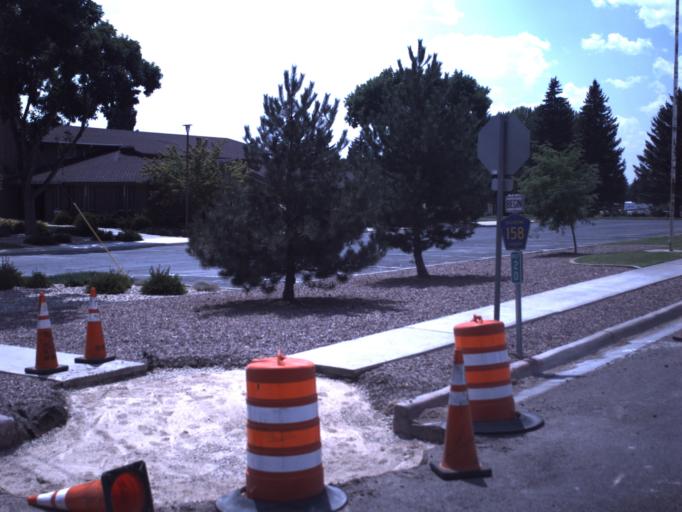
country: US
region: Utah
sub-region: Duchesne County
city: Roosevelt
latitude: 40.4329
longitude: -110.0301
